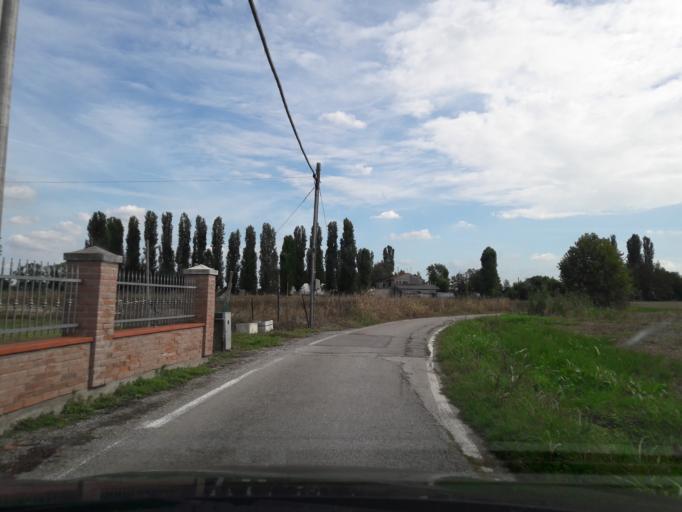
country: IT
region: Veneto
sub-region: Provincia di Padova
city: Piacenza d'Adige
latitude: 45.0889
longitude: 11.5521
